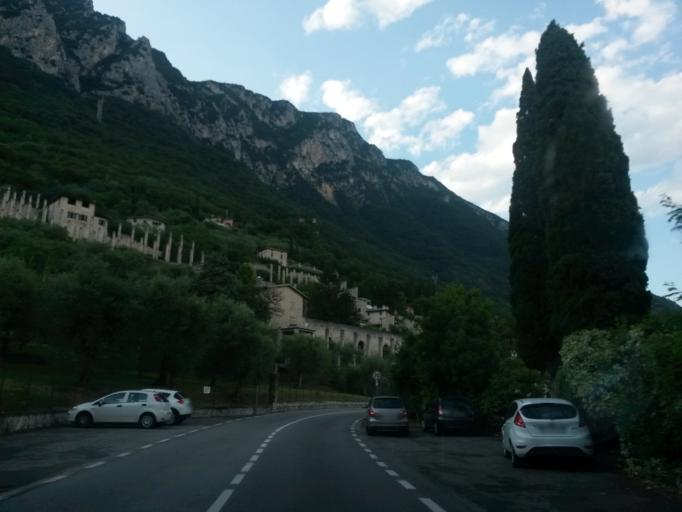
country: IT
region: Lombardy
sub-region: Provincia di Brescia
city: Gargnano
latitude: 45.6931
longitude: 10.6672
